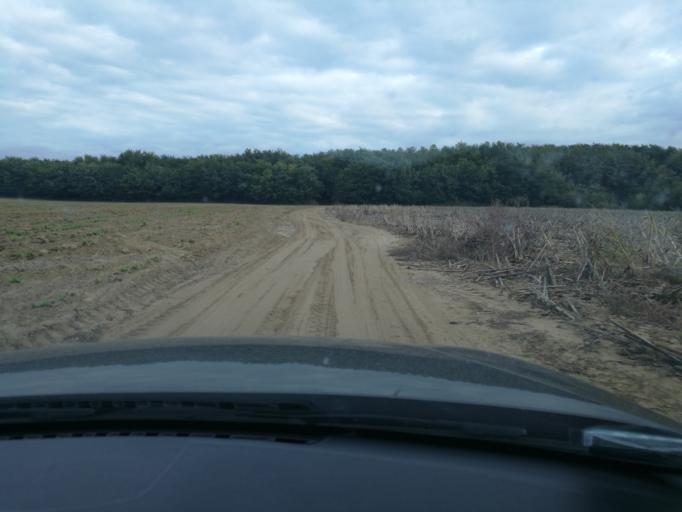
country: HU
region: Szabolcs-Szatmar-Bereg
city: Apagy
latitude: 47.9976
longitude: 21.9103
